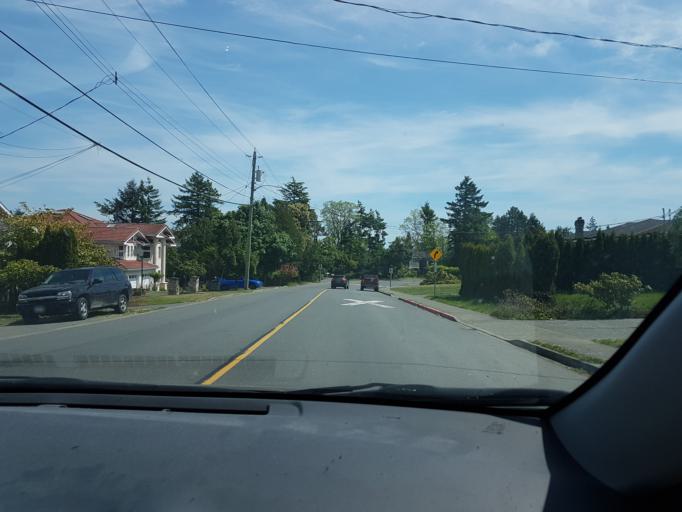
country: CA
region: British Columbia
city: Oak Bay
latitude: 48.4852
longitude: -123.3077
